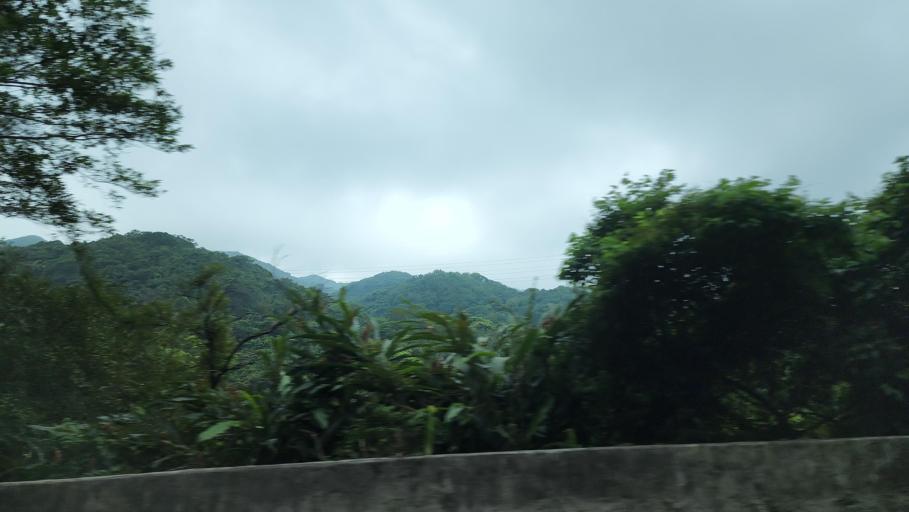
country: TW
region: Taiwan
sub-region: Keelung
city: Keelung
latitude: 25.1665
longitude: 121.6804
